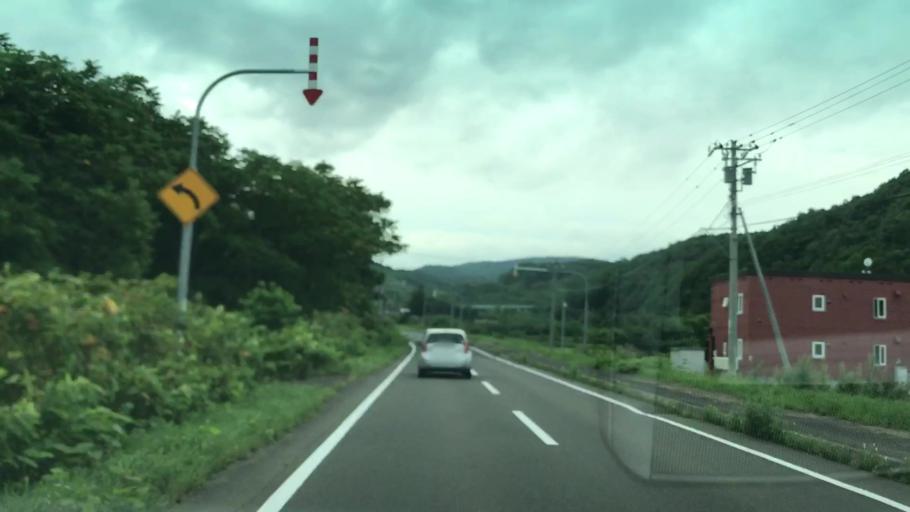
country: JP
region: Hokkaido
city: Yoichi
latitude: 43.1537
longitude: 140.8216
